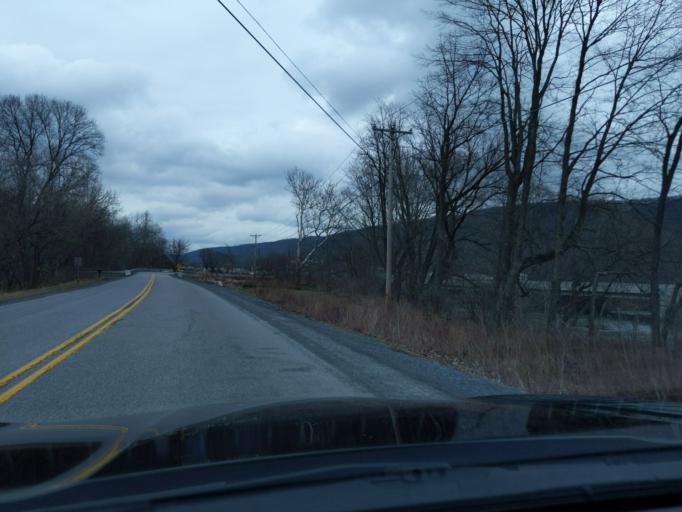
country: US
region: Pennsylvania
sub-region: Blair County
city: Tipton
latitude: 40.6277
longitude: -78.2962
